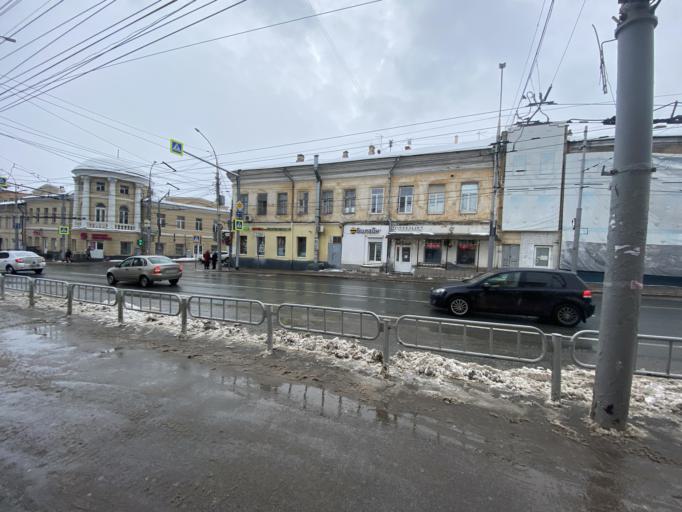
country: RU
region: Saratov
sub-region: Saratovskiy Rayon
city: Saratov
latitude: 51.5294
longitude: 46.0520
